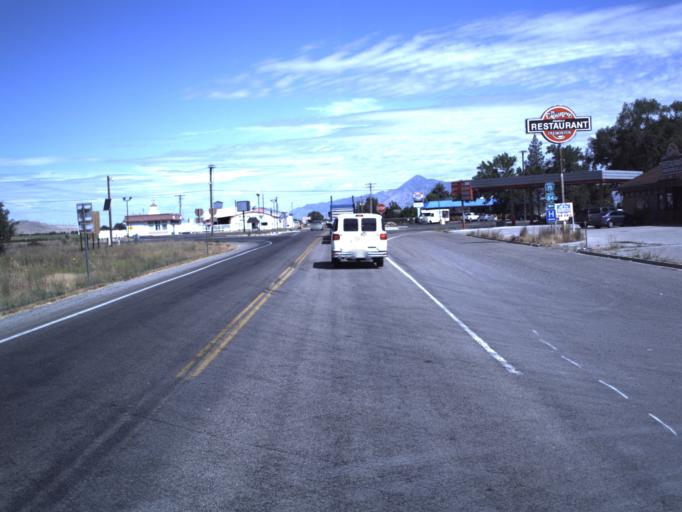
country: US
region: Utah
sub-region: Box Elder County
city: Elwood
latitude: 41.7111
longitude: -112.1422
